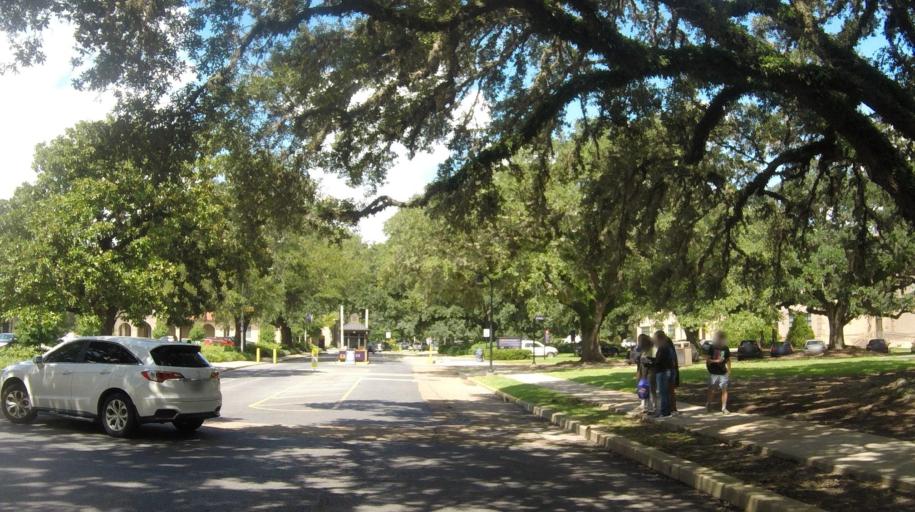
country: US
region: Louisiana
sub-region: East Baton Rouge Parish
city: Baton Rouge
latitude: 30.4158
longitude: -91.1781
